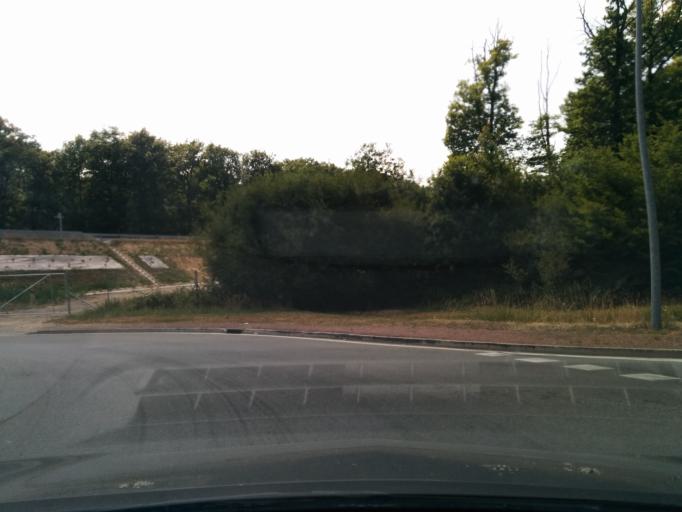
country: FR
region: Centre
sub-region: Departement du Cher
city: Vierzon
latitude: 47.2489
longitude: 2.0606
